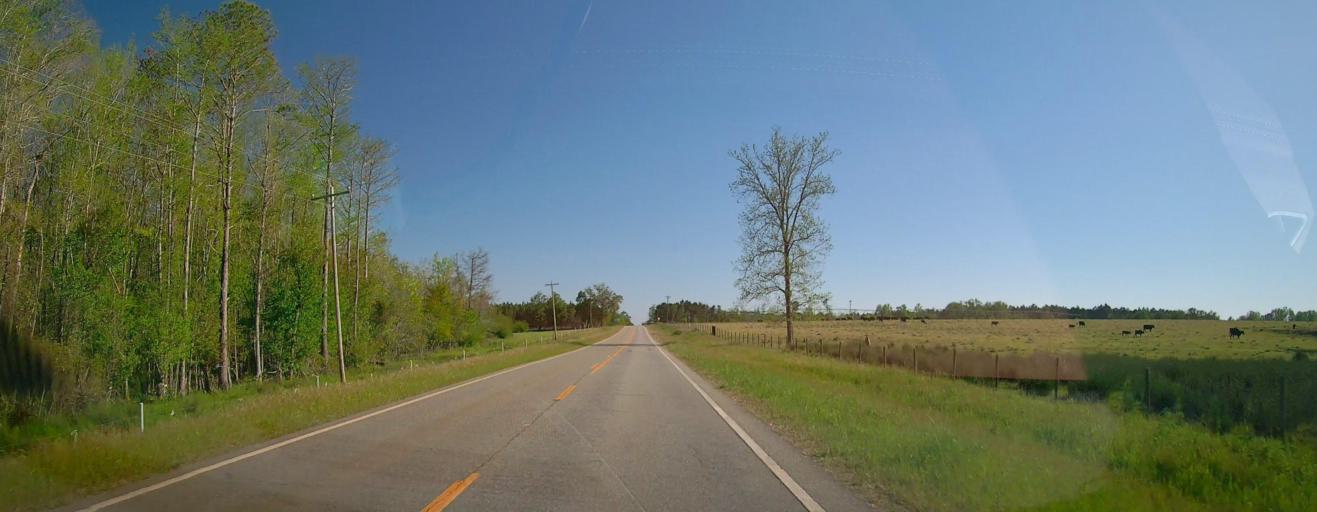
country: US
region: Georgia
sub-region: Wilcox County
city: Rochelle
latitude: 31.8501
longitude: -83.4890
